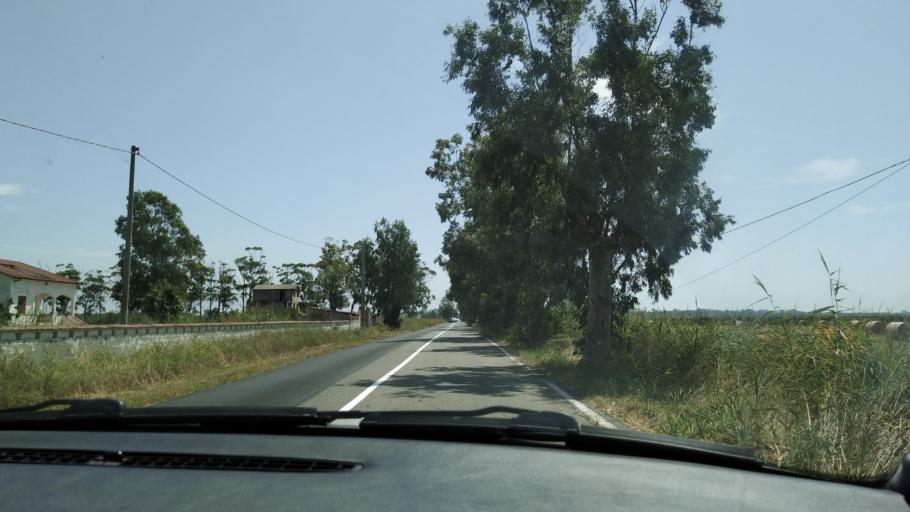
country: IT
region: Basilicate
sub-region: Provincia di Matera
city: Marconia
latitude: 40.3331
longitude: 16.7779
